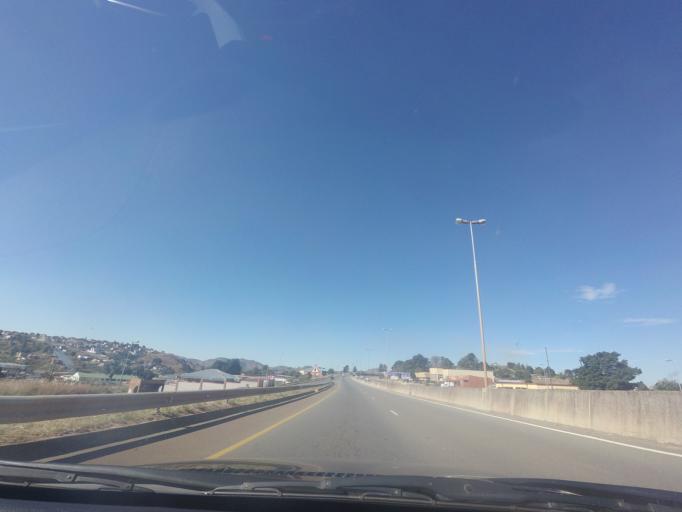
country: SZ
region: Hhohho
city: Mbabane
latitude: -26.2993
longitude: 31.1158
